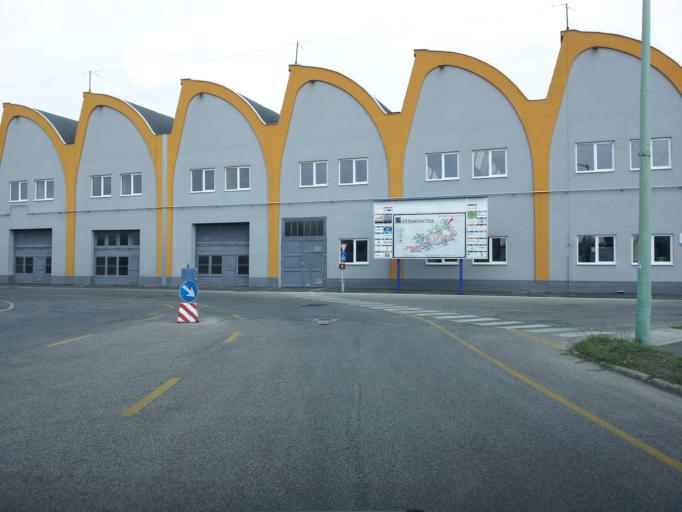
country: HU
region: Pest
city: Szigethalom
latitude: 47.3287
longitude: 19.0083
